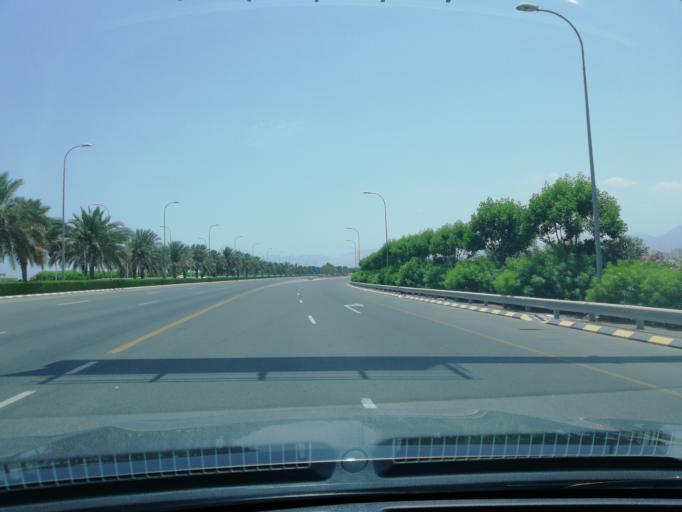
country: OM
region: Muhafazat Masqat
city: Bawshar
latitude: 23.6025
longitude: 58.3224
